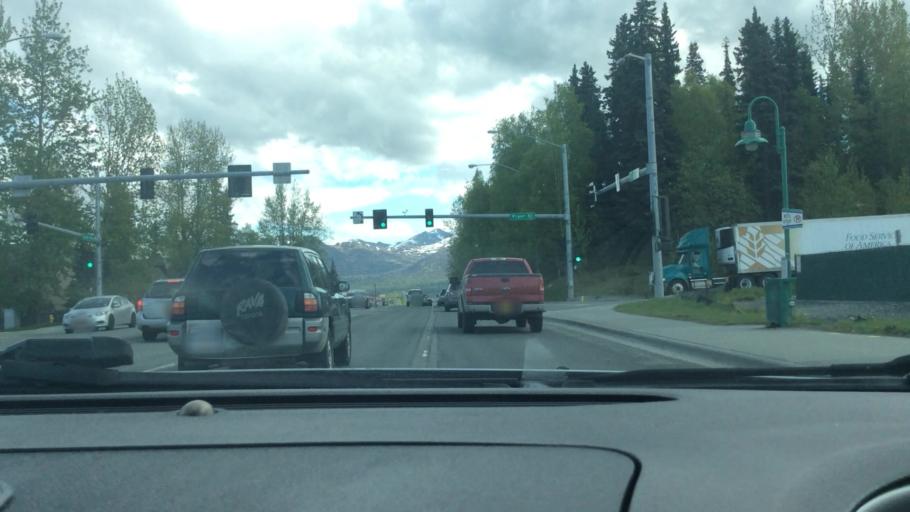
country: US
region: Alaska
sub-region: Anchorage Municipality
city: Anchorage
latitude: 61.1808
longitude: -149.8243
